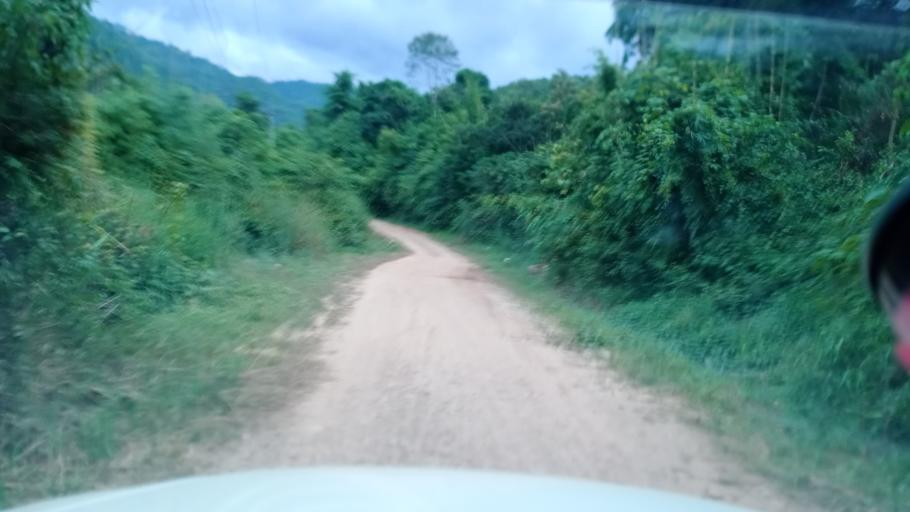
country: TH
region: Changwat Bueng Kan
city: Pak Khat
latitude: 18.7234
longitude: 103.2522
